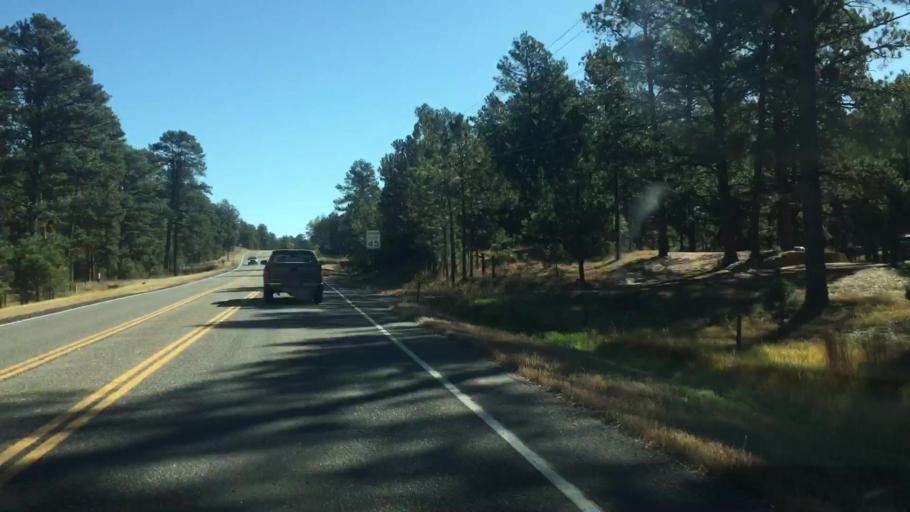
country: US
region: Colorado
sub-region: Elbert County
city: Elizabeth
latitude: 39.3615
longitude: -104.5832
